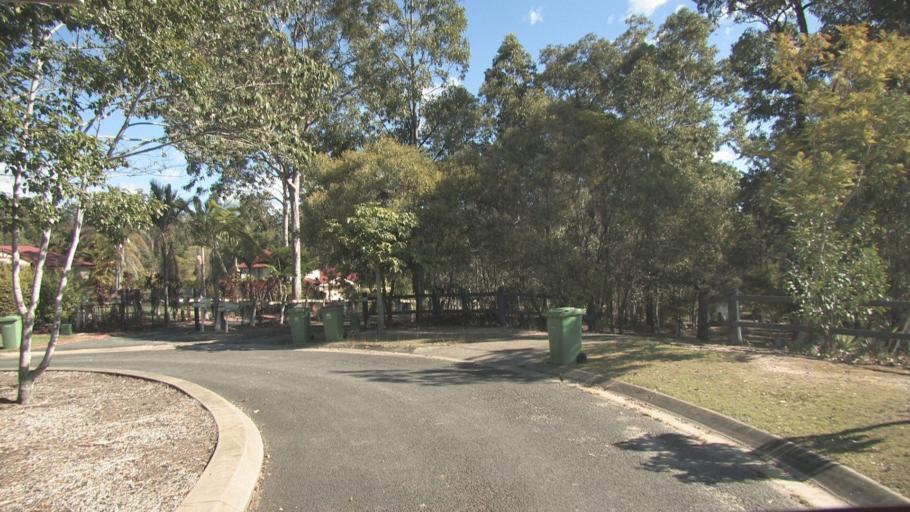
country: AU
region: Queensland
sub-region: Ipswich
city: Springfield Lakes
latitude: -27.7354
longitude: 152.9154
